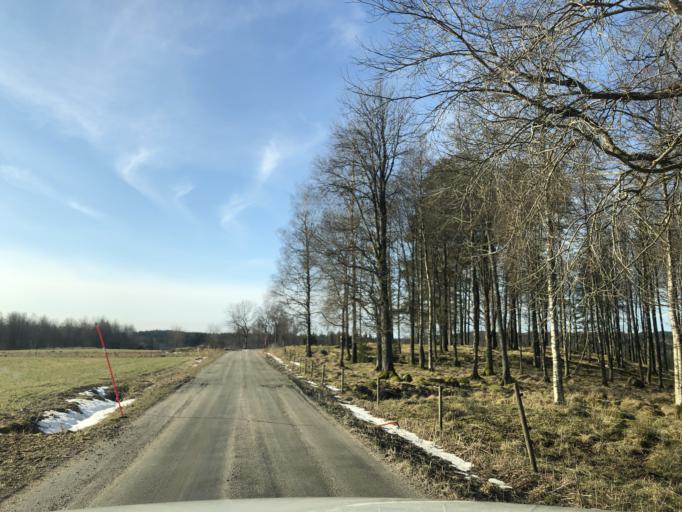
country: SE
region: Vaestra Goetaland
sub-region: Ulricehamns Kommun
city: Ulricehamn
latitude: 57.7981
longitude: 13.4907
